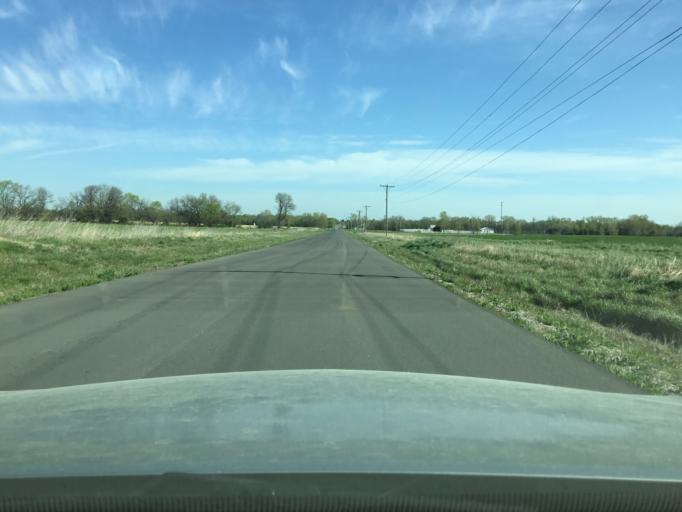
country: US
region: Kansas
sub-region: Neosho County
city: Chanute
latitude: 37.6506
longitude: -95.4435
